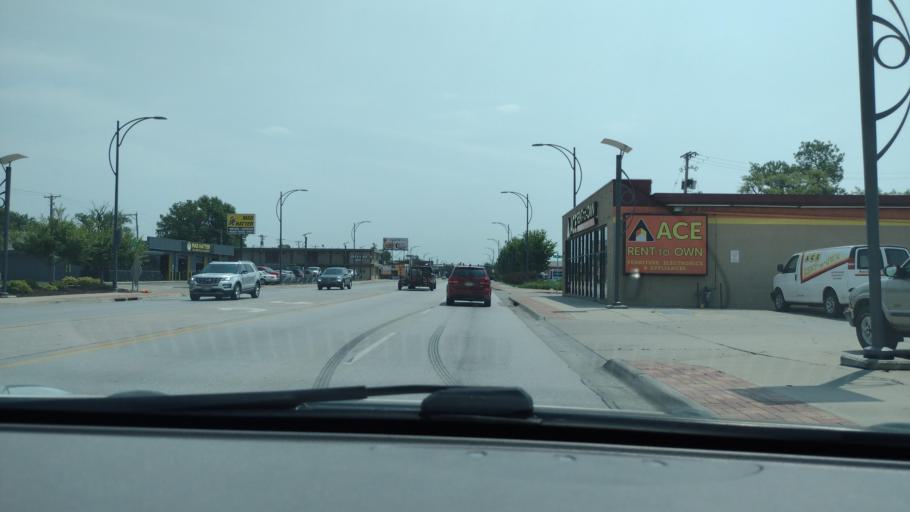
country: US
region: Iowa
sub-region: Pottawattamie County
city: Carter Lake
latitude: 41.2619
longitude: -95.9000
